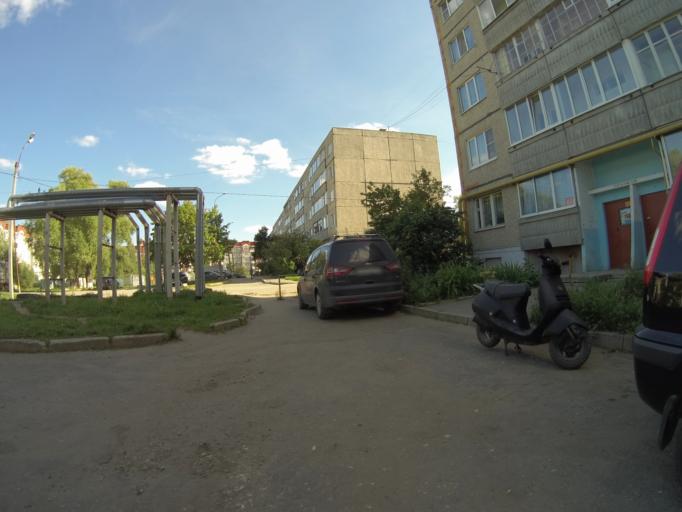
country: RU
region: Vladimir
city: Vorsha
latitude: 56.0958
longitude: 40.1941
